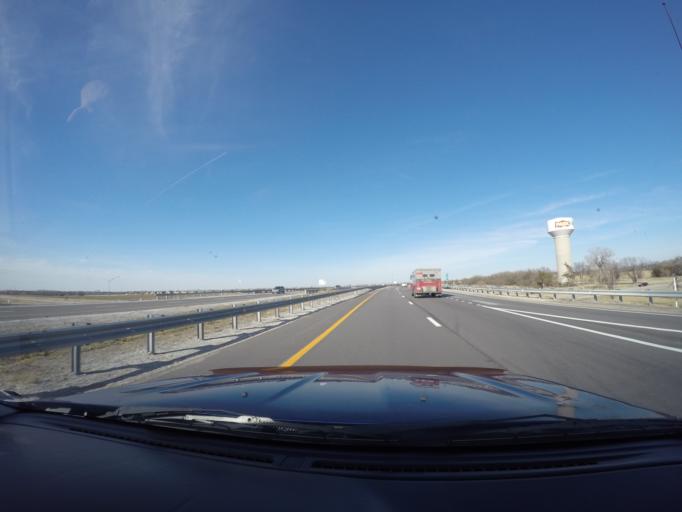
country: US
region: Kansas
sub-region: Sedgwick County
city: Park City
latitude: 37.8384
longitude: -97.3277
